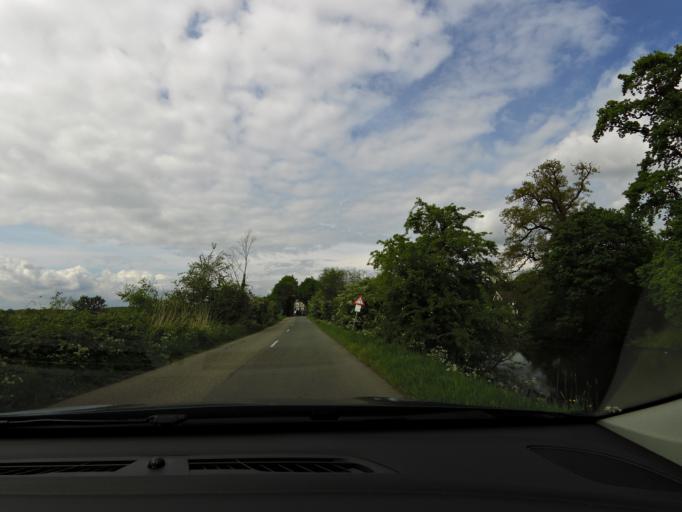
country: NL
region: Utrecht
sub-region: Gemeente Utrechtse Heuvelrug
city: Amerongen
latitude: 51.9951
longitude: 5.4567
